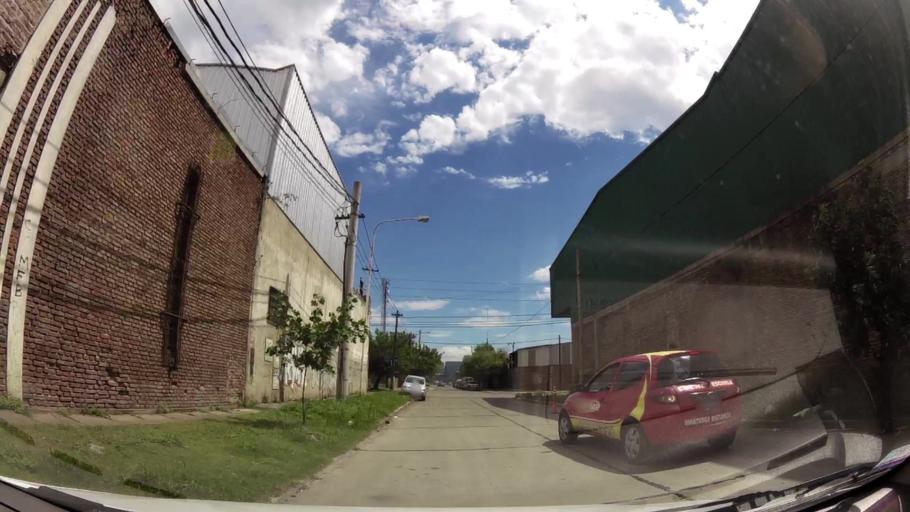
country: AR
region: Buenos Aires
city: San Justo
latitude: -34.6805
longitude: -58.5472
